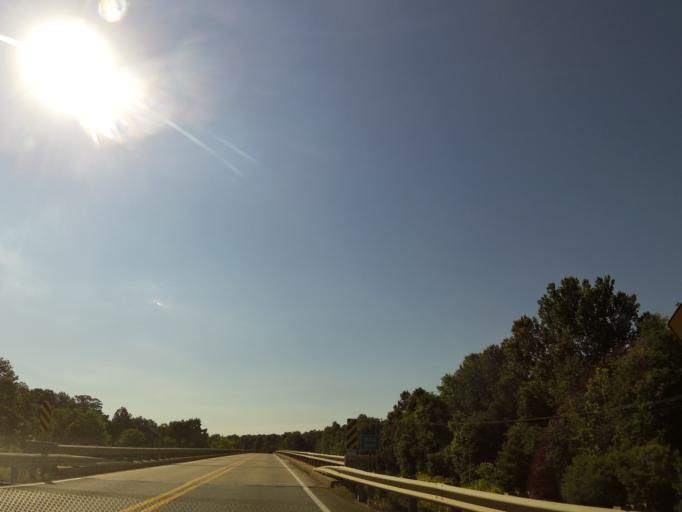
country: US
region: Arkansas
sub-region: Clay County
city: Corning
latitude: 36.4028
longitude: -90.5432
